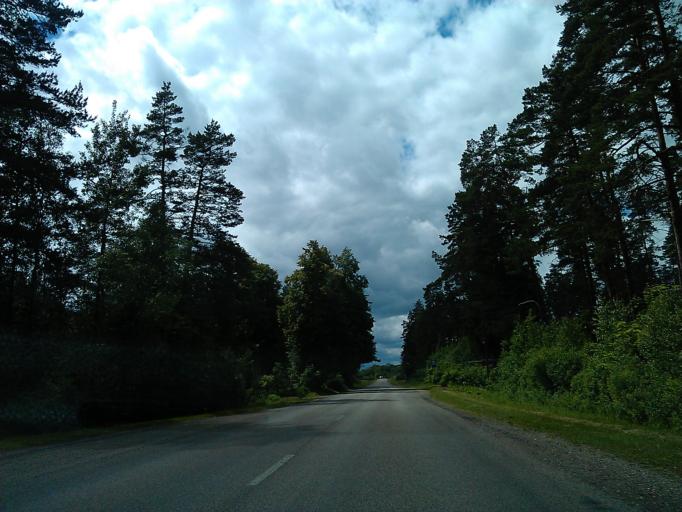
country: LV
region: Talsu Rajons
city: Stende
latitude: 57.0837
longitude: 22.3010
